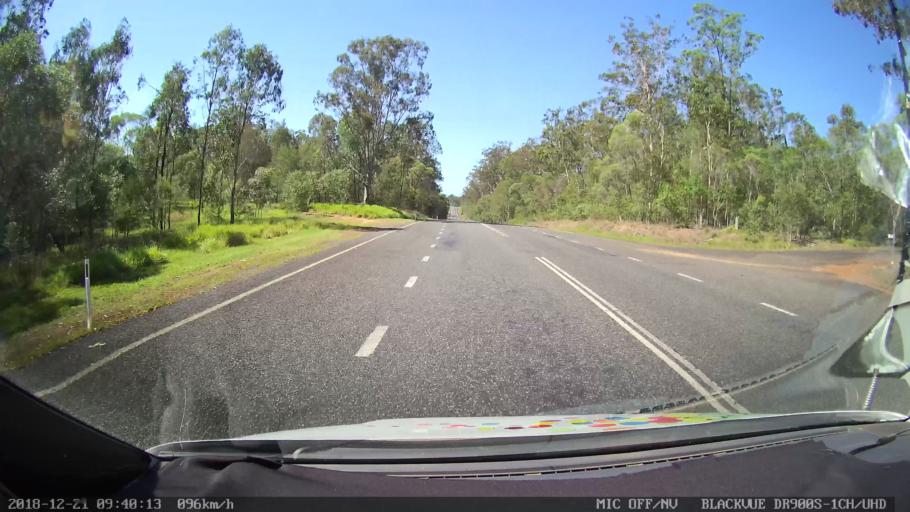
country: AU
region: New South Wales
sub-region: Clarence Valley
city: Grafton
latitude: -29.5694
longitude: 152.9642
